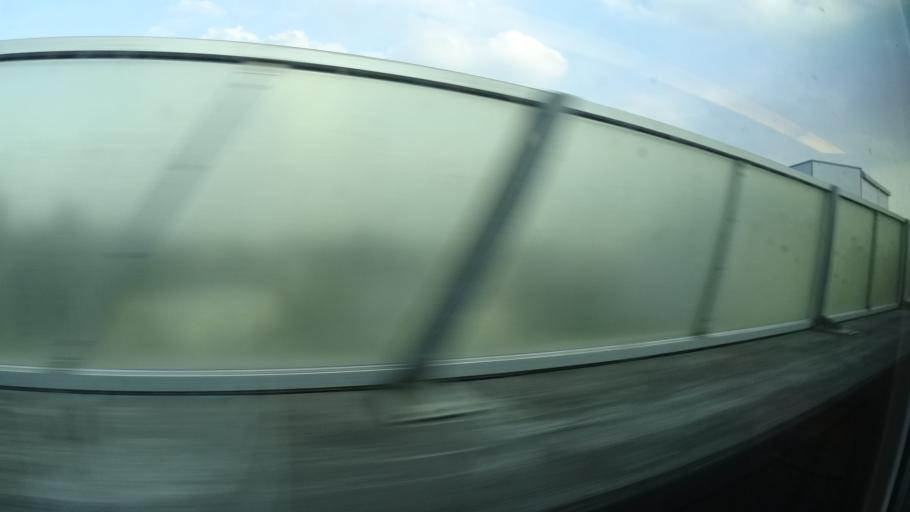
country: JP
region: Saitama
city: Ageoshimo
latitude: 35.9896
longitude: 139.6311
